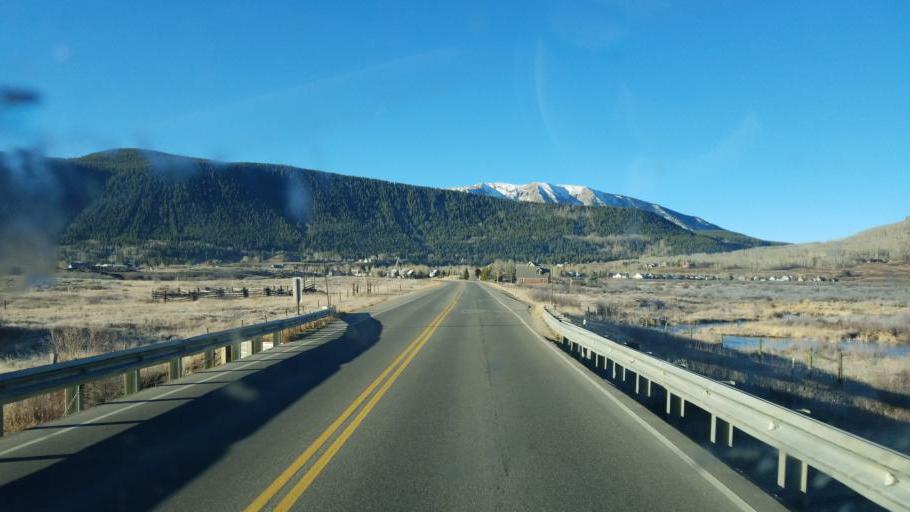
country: US
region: Colorado
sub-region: Gunnison County
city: Crested Butte
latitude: 38.8773
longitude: -106.9770
